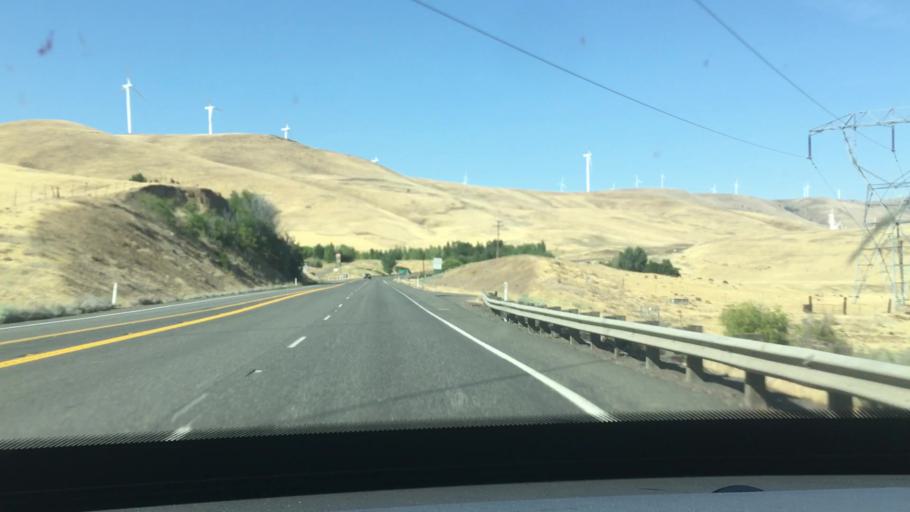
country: US
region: Washington
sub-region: Klickitat County
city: Goldendale
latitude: 45.6999
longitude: -120.8236
